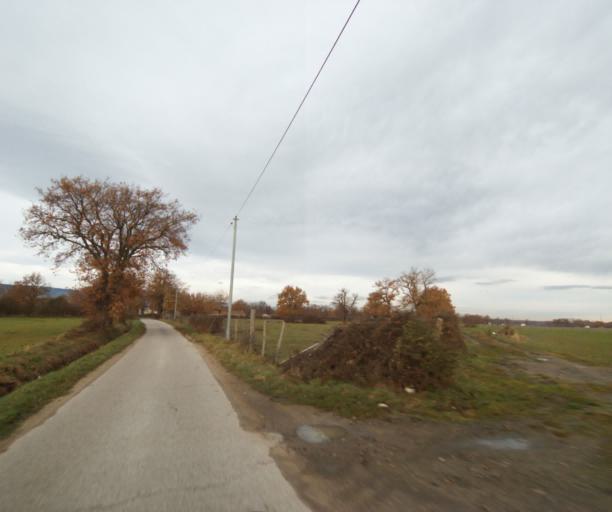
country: FR
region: Rhone-Alpes
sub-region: Departement de la Loire
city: Sury-le-Comtal
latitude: 45.5460
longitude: 4.1652
